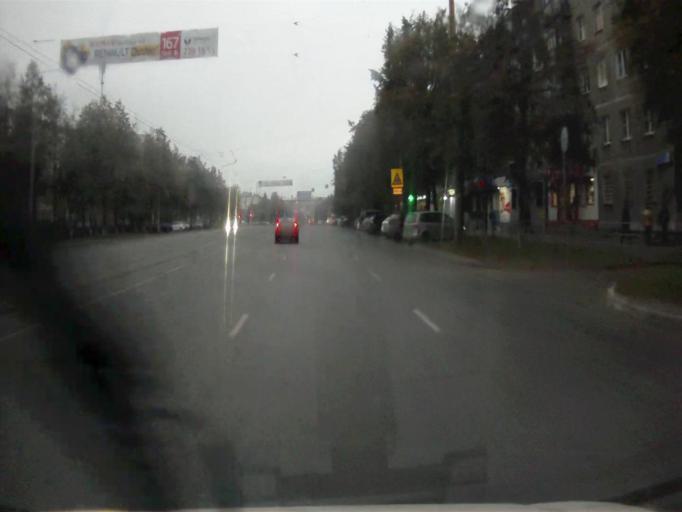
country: RU
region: Chelyabinsk
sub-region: Gorod Chelyabinsk
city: Chelyabinsk
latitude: 55.1772
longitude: 61.3997
